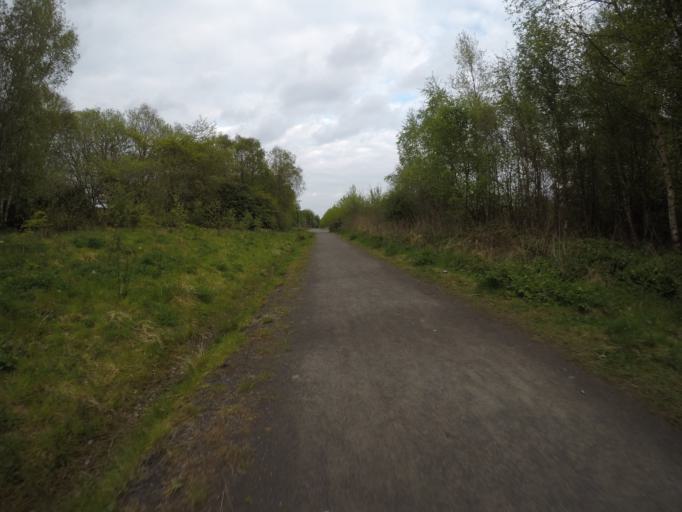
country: GB
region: Scotland
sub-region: North Ayrshire
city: Irvine
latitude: 55.6298
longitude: -4.6540
